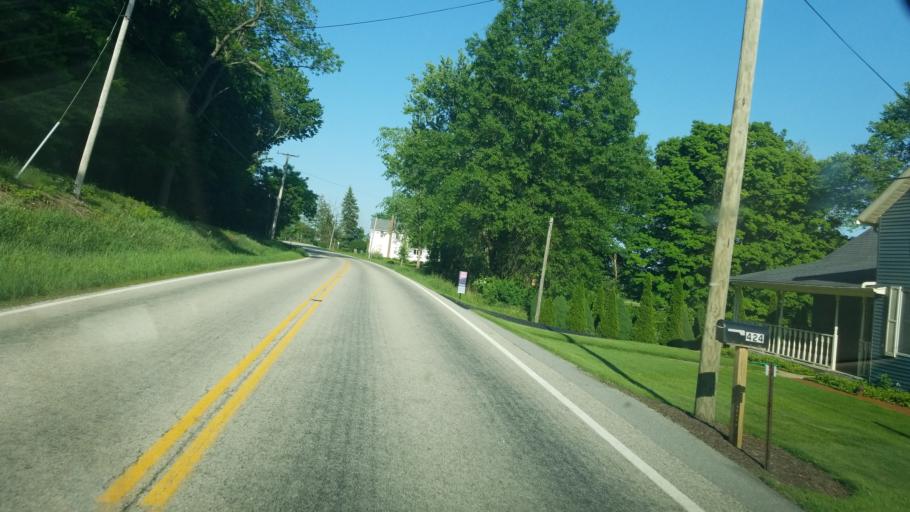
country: US
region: Ohio
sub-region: Medina County
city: Wadsworth
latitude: 41.0922
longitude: -81.7030
